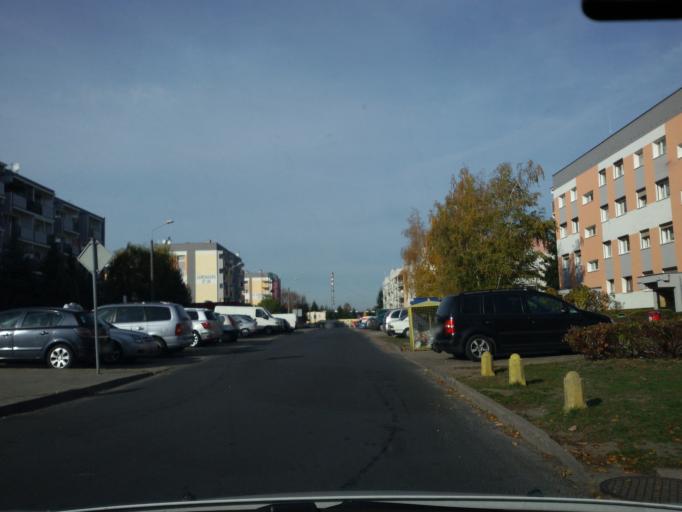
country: PL
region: Greater Poland Voivodeship
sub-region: Leszno
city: Leszno
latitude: 51.8331
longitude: 16.6008
